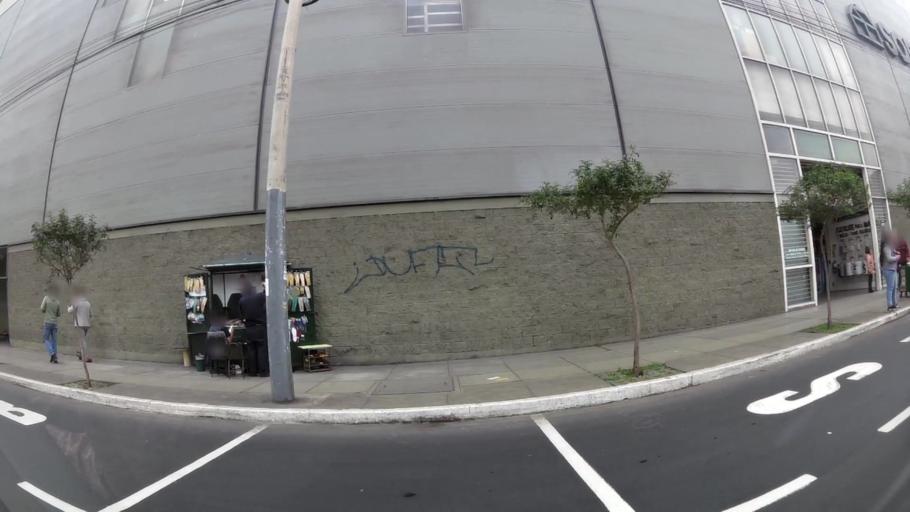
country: PE
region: Lima
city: Lima
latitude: -12.0485
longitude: -77.0389
